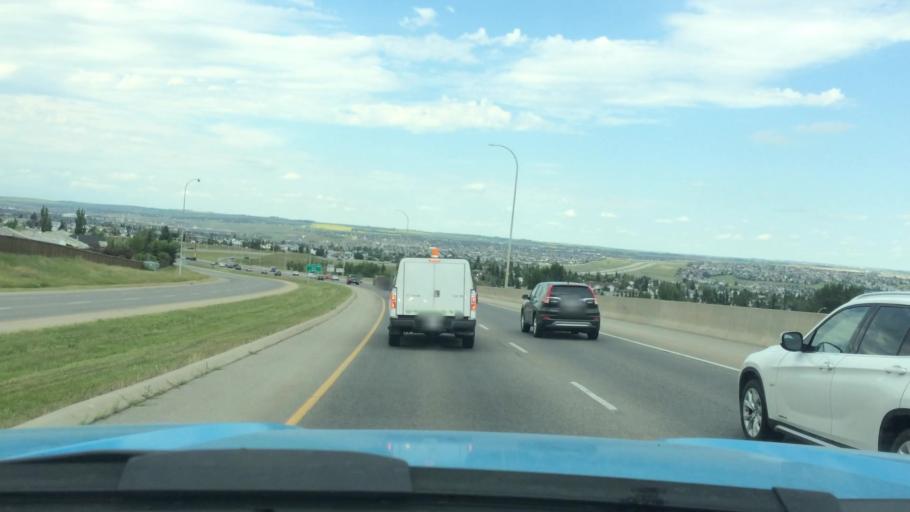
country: CA
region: Alberta
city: Calgary
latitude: 51.1374
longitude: -114.1209
